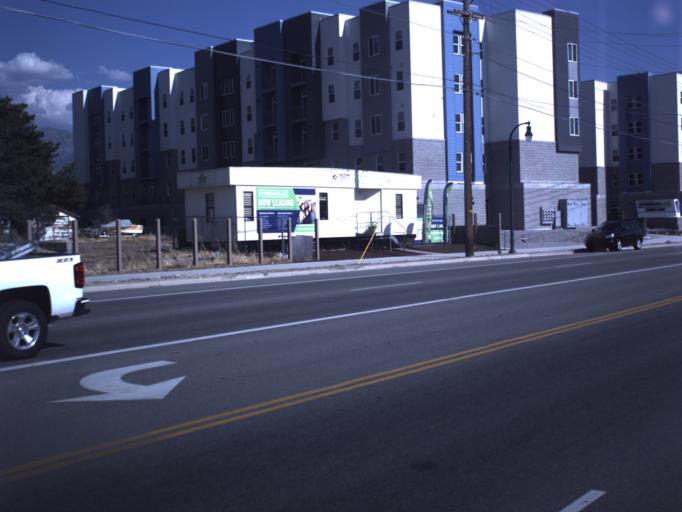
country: US
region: Utah
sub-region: Utah County
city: Orem
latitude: 40.2822
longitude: -111.7321
